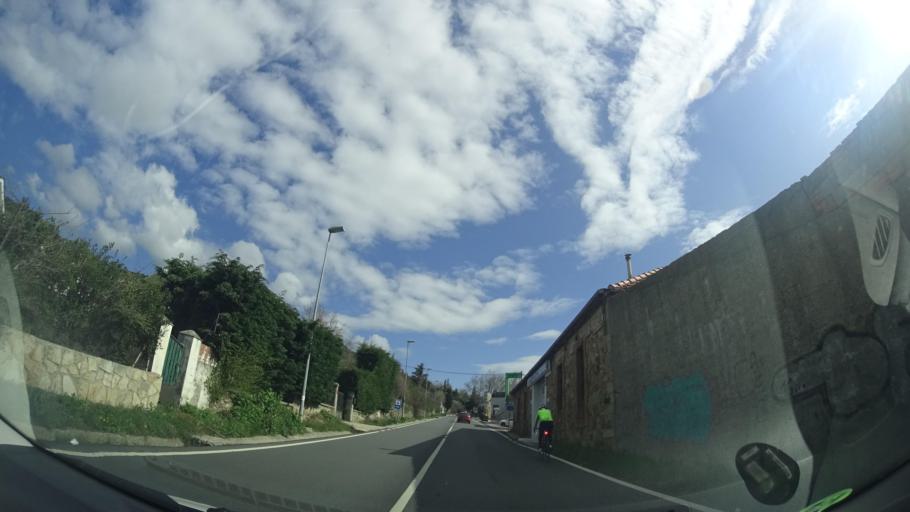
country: ES
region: Madrid
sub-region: Provincia de Madrid
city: Miraflores de la Sierra
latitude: 40.8105
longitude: -3.7699
